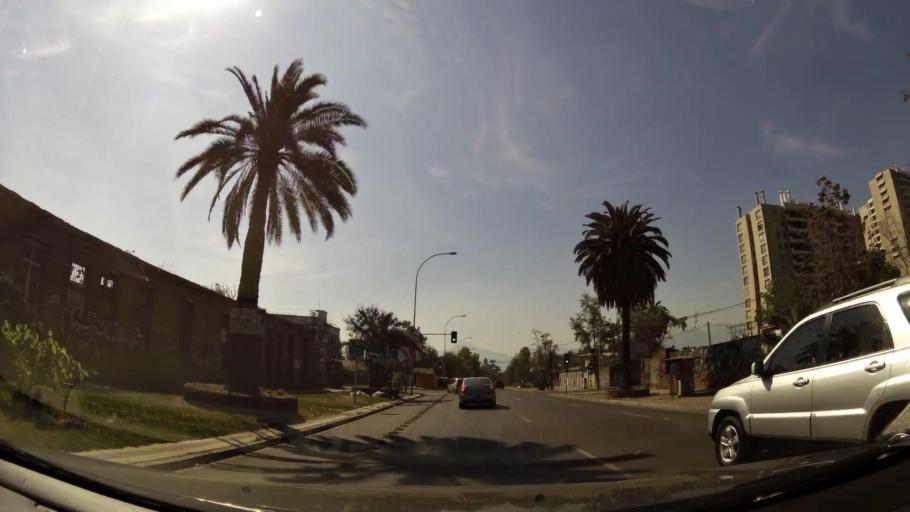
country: CL
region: Santiago Metropolitan
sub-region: Provincia de Santiago
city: Santiago
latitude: -33.4217
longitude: -70.6508
